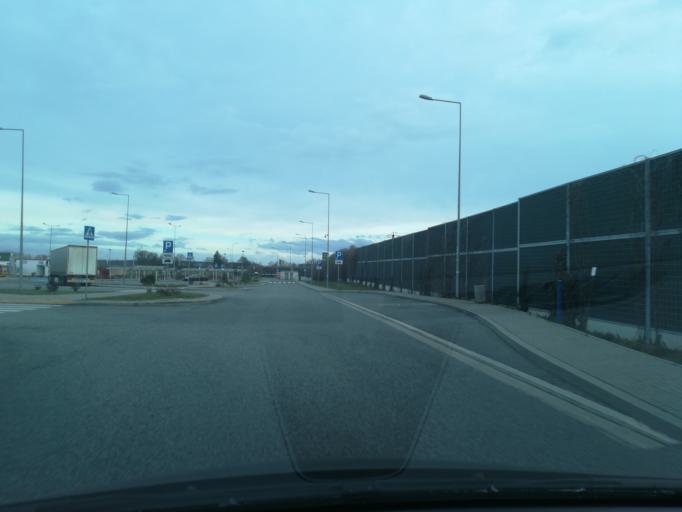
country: PL
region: Kujawsko-Pomorskie
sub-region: Powiat wloclawski
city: Brzesc Kujawski
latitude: 52.6552
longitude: 18.9281
